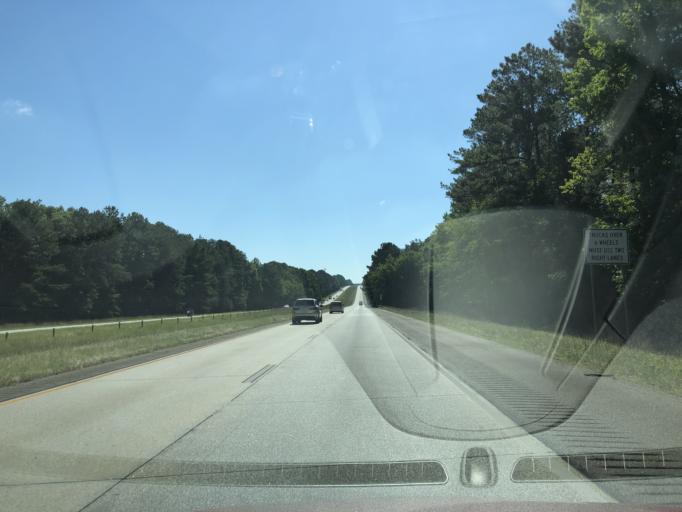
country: US
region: Georgia
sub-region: McDuffie County
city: Thomson
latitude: 33.5070
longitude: -82.5392
